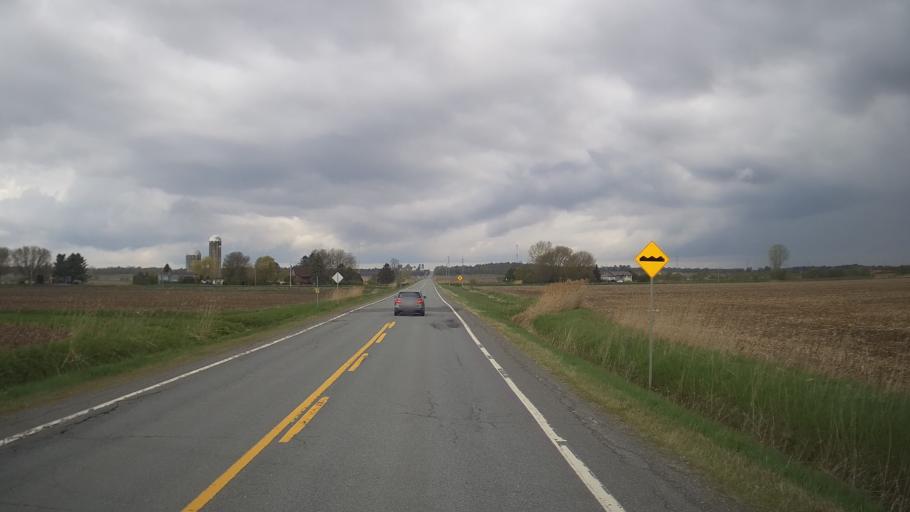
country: CA
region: Quebec
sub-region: Monteregie
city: Farnham
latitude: 45.2567
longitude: -72.9158
